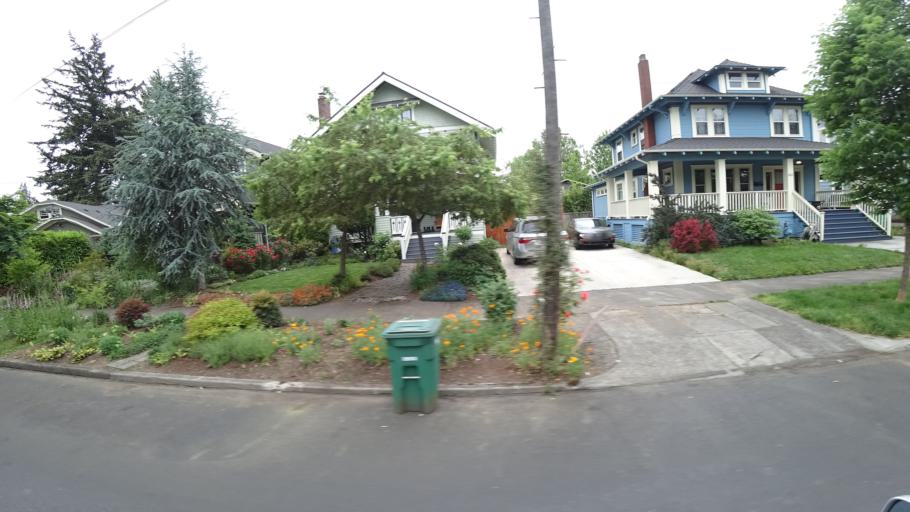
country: US
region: Oregon
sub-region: Multnomah County
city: Portland
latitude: 45.5430
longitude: -122.6067
